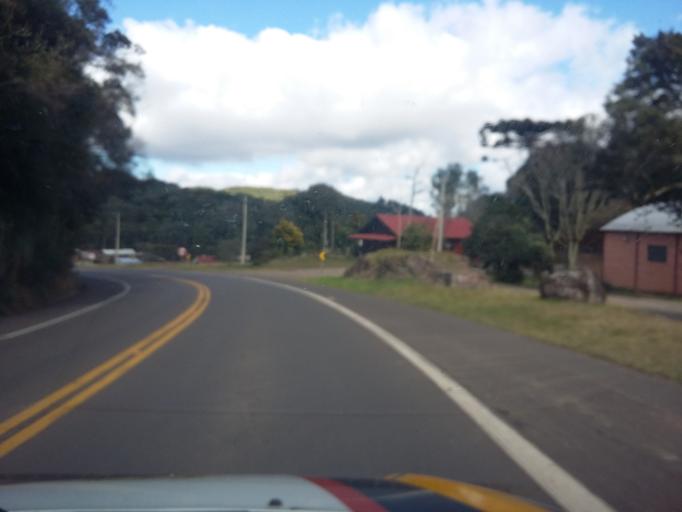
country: BR
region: Rio Grande do Sul
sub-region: Sao Marcos
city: Sao Marcos
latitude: -28.7906
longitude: -51.0964
